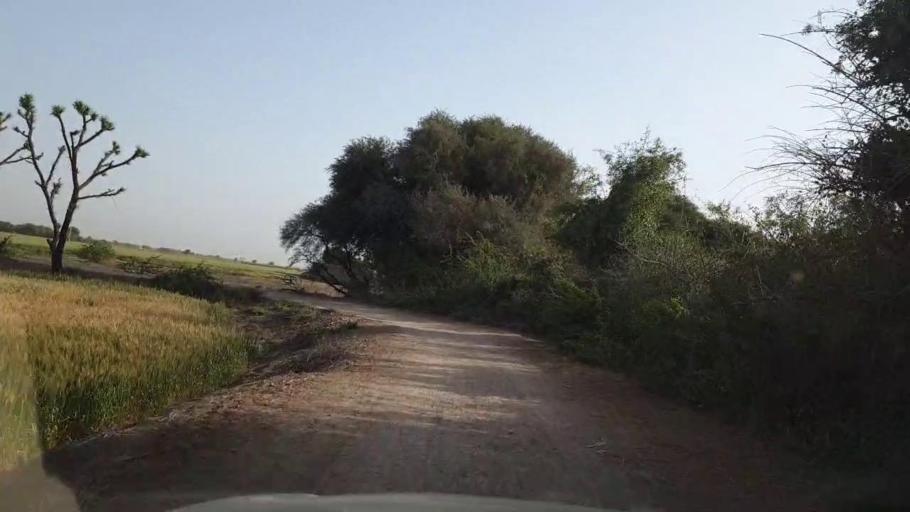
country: PK
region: Sindh
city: Tando Ghulam Ali
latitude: 25.0822
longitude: 68.8847
